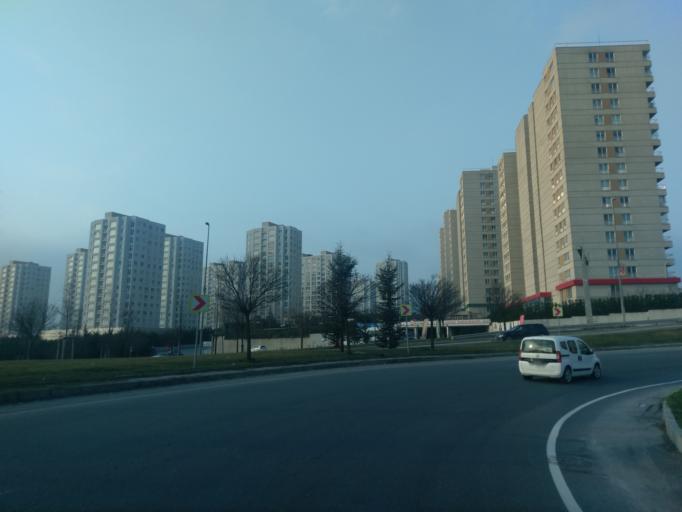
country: TR
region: Istanbul
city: Esenyurt
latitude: 41.0593
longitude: 28.7063
